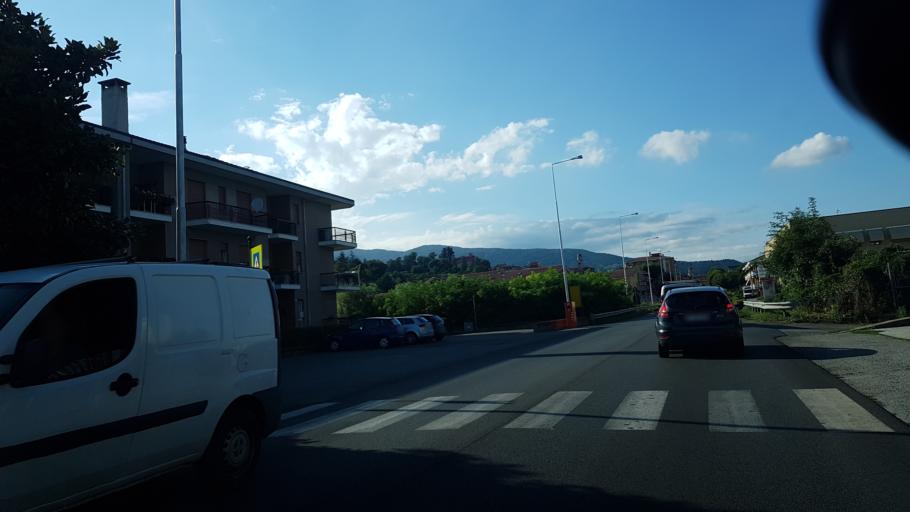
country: IT
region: Piedmont
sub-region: Provincia di Cuneo
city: Costiglione Saluzzo
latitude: 44.5579
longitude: 7.4893
